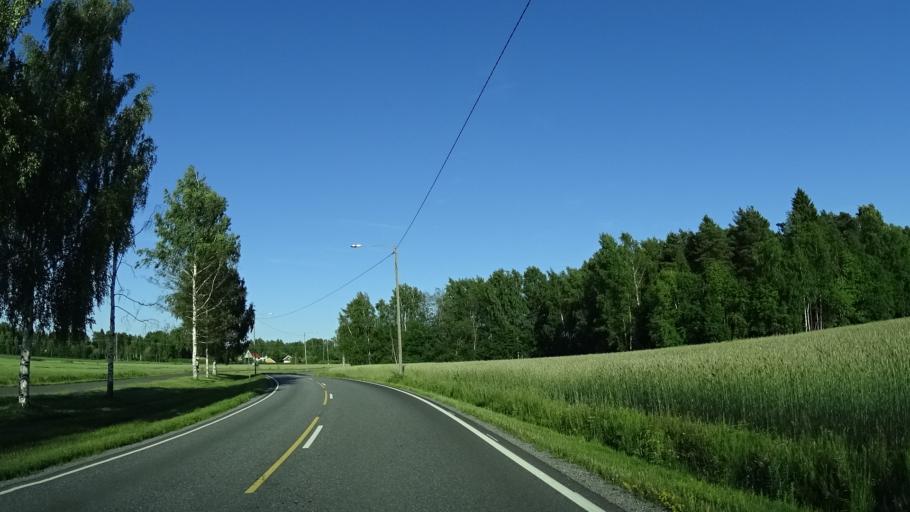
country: FI
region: Satakunta
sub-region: Pori
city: Harjavalta
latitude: 61.3462
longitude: 22.1028
